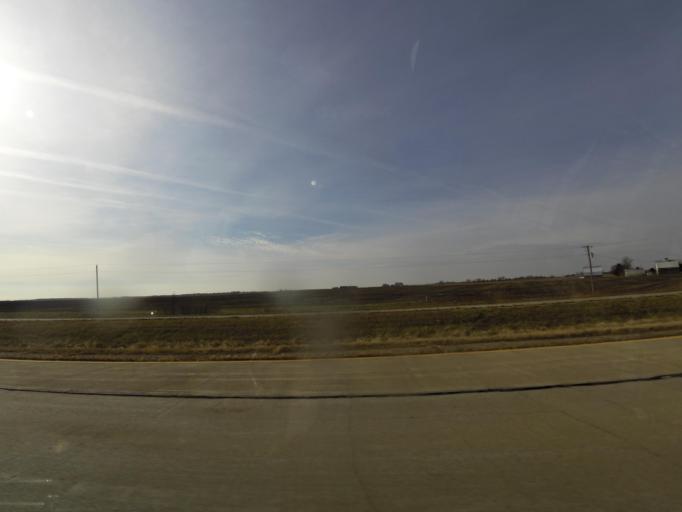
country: US
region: Illinois
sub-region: McLean County
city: Heyworth
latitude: 40.2967
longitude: -88.9787
